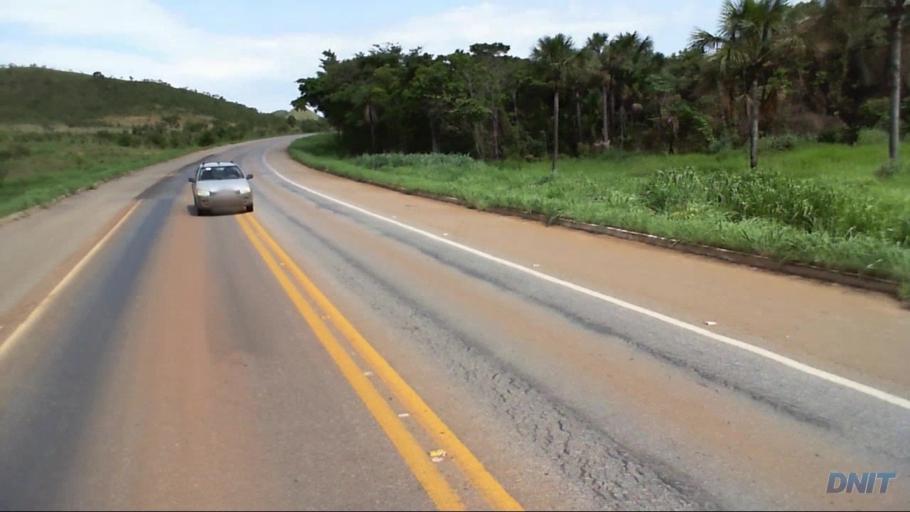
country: BR
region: Goias
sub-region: Barro Alto
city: Barro Alto
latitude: -15.1778
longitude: -48.7923
